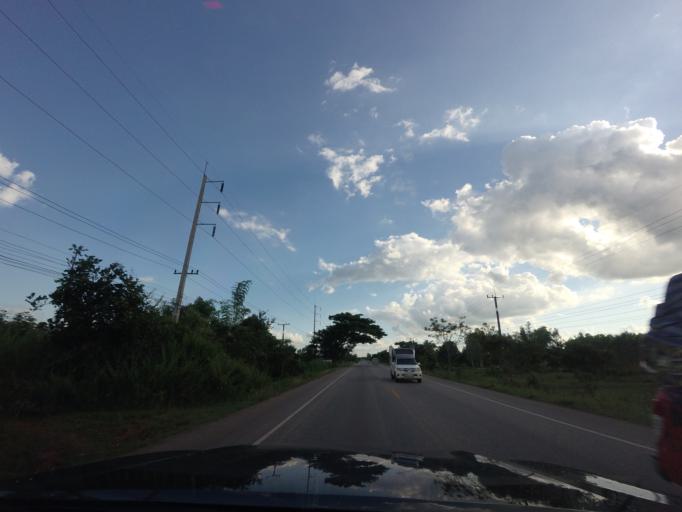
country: TH
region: Changwat Udon Thani
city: Thung Fon
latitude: 17.4746
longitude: 103.1942
